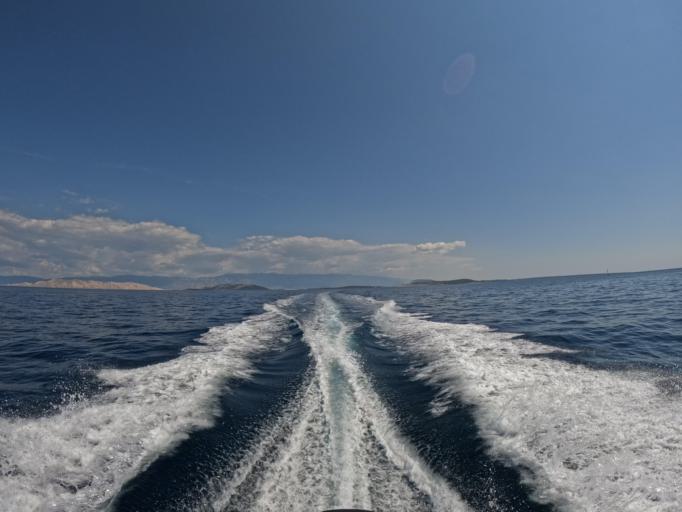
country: HR
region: Primorsko-Goranska
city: Lopar
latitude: 44.8848
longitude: 14.6429
